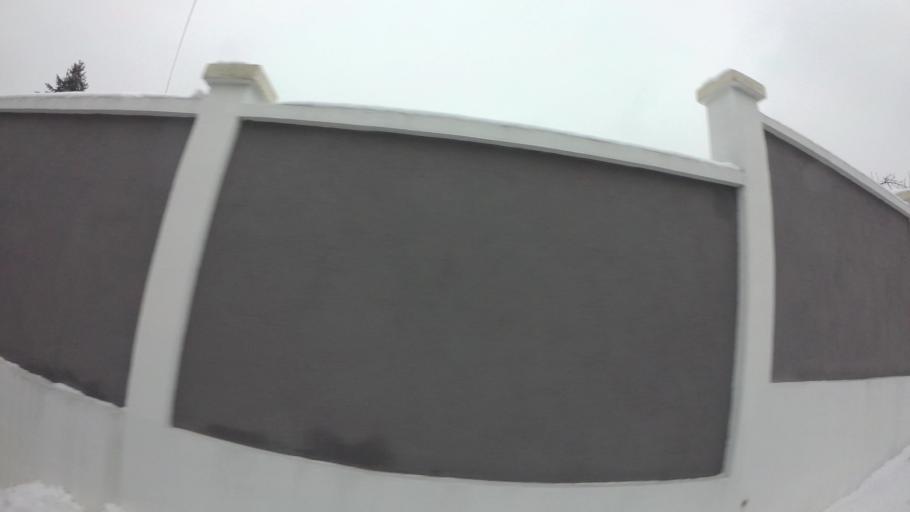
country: BA
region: Federation of Bosnia and Herzegovina
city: Hadzici
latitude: 43.8476
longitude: 18.2578
